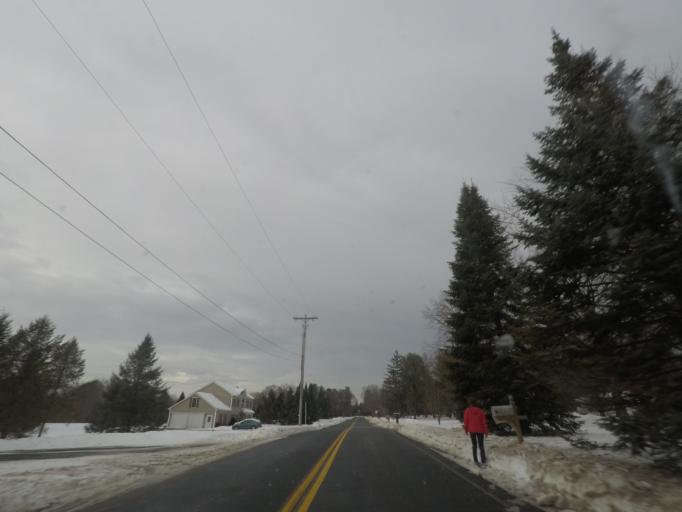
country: US
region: New York
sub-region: Rensselaer County
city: Castleton-on-Hudson
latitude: 42.5155
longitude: -73.6922
